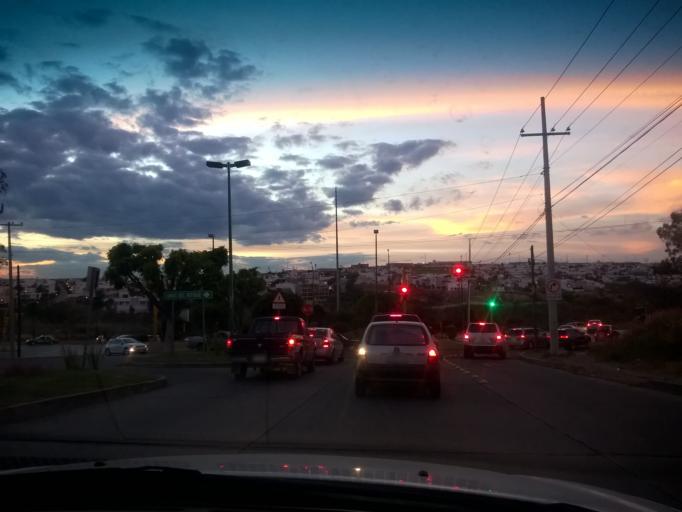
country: MX
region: Guanajuato
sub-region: Leon
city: La Ermita
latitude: 21.1518
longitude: -101.7199
